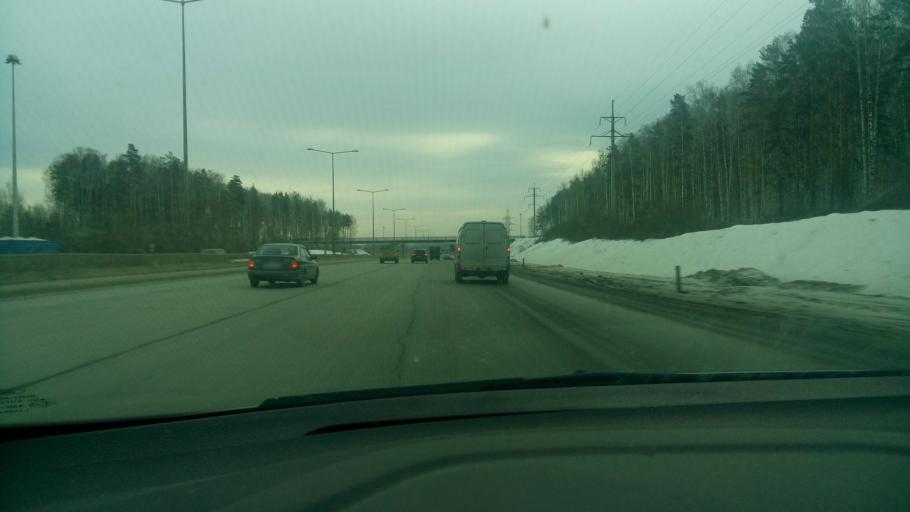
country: RU
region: Sverdlovsk
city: Istok
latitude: 56.7708
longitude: 60.7282
